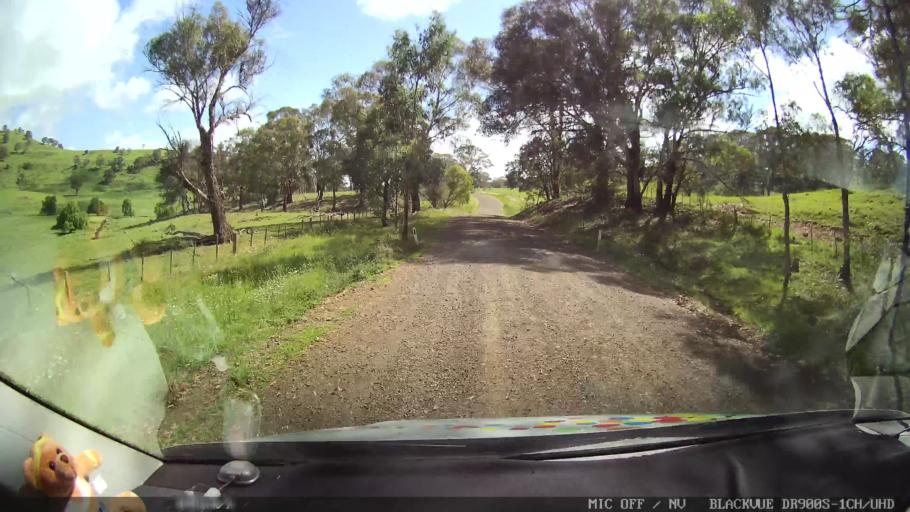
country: AU
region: New South Wales
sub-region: Guyra
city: Guyra
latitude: -29.9910
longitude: 151.6867
